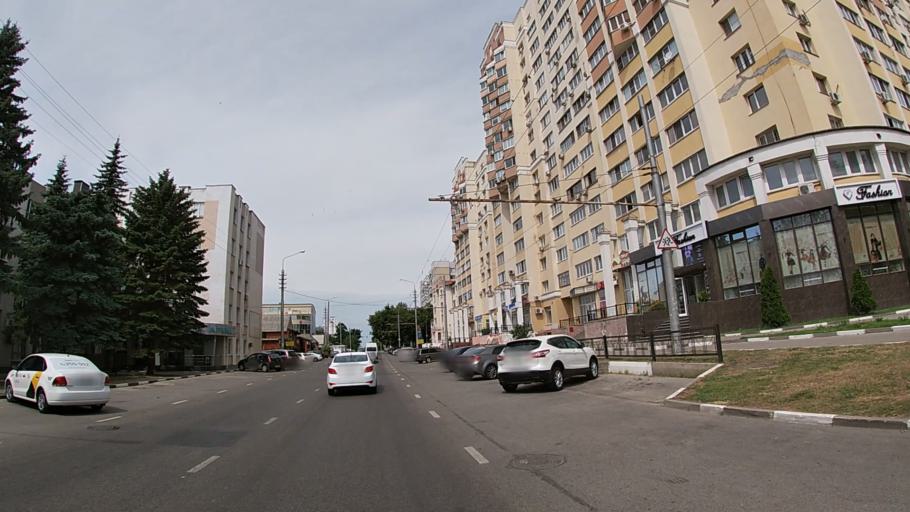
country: RU
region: Belgorod
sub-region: Belgorodskiy Rayon
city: Belgorod
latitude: 50.6003
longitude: 36.5774
